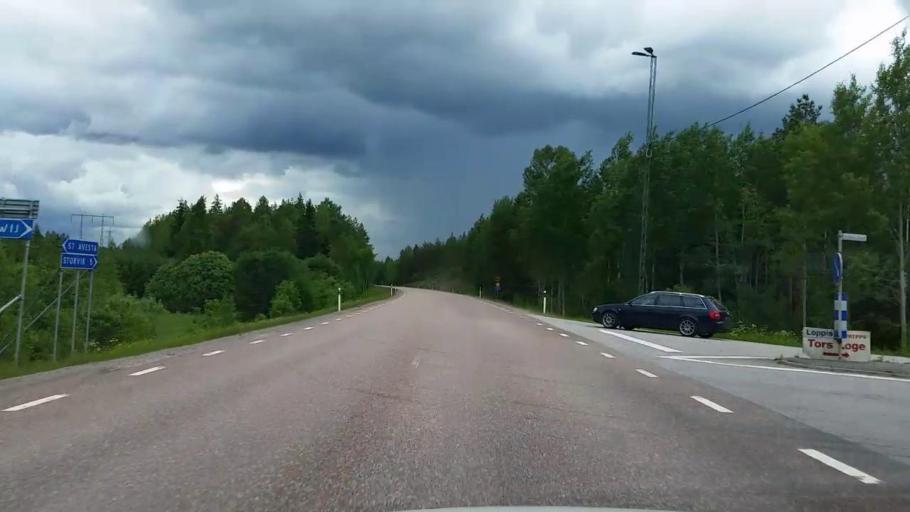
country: SE
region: Gaevleborg
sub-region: Hofors Kommun
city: Hofors
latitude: 60.5485
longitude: 16.4736
